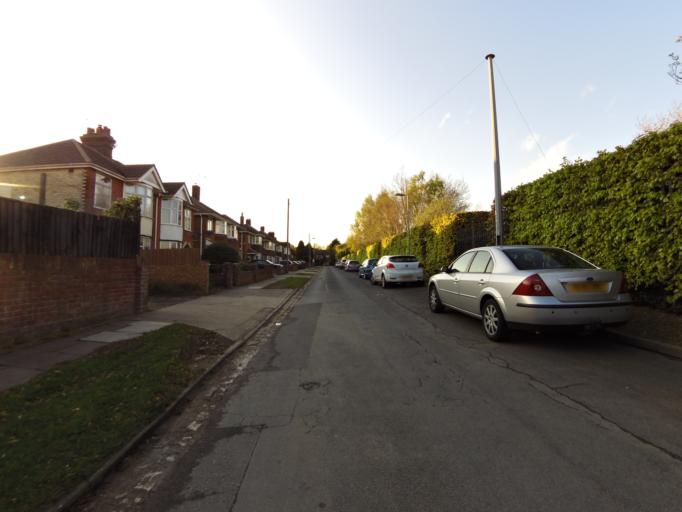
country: GB
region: England
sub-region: Suffolk
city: Ipswich
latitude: 52.0709
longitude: 1.1784
